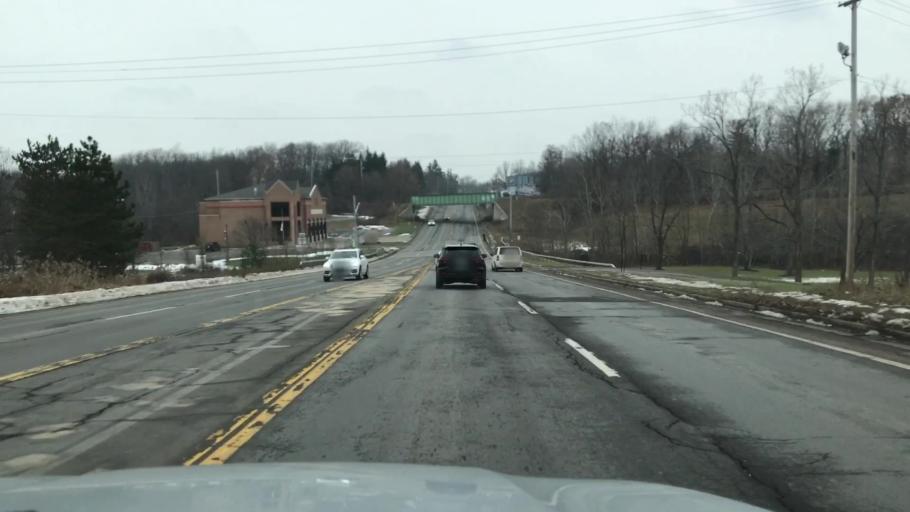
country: US
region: New York
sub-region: Erie County
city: Blasdell
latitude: 42.7900
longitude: -78.7922
